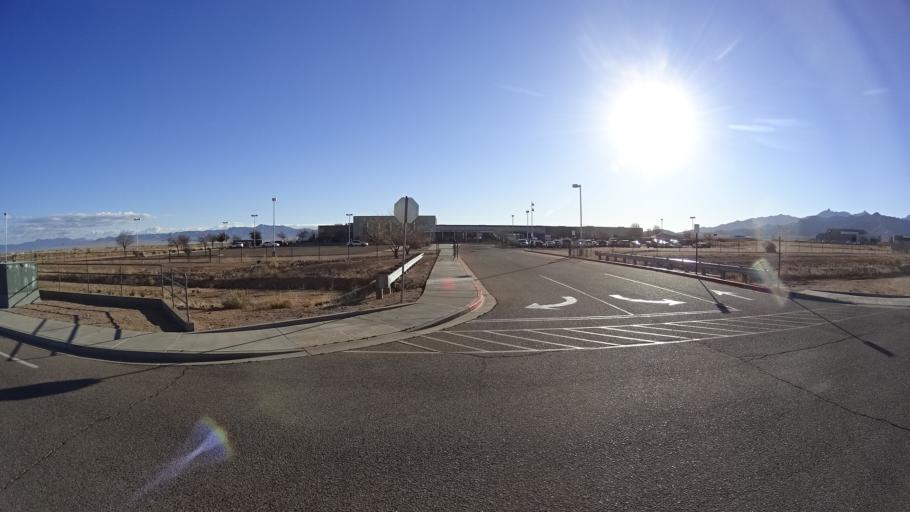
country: US
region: Arizona
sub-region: Mohave County
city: New Kingman-Butler
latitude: 35.2293
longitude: -113.9761
